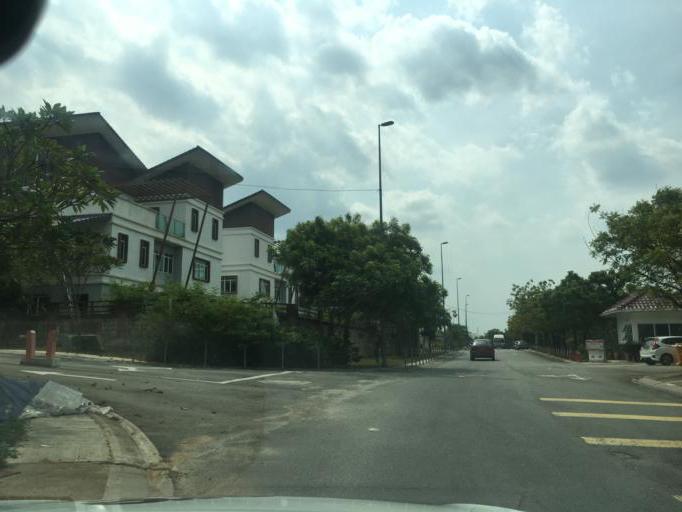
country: MY
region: Selangor
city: Shah Alam
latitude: 3.0807
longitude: 101.4800
